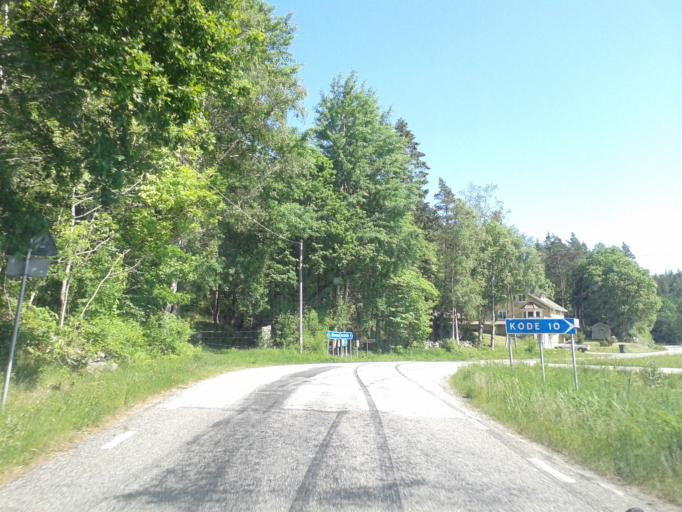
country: SE
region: Vaestra Goetaland
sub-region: Kungalvs Kommun
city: Diserod
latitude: 57.9746
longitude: 11.9713
